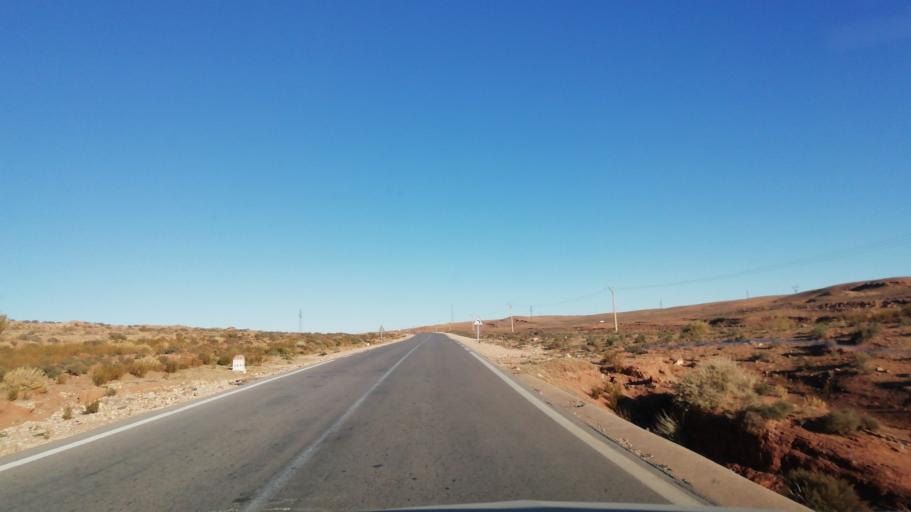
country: DZ
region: El Bayadh
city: El Abiodh Sidi Cheikh
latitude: 33.1687
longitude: 0.4278
